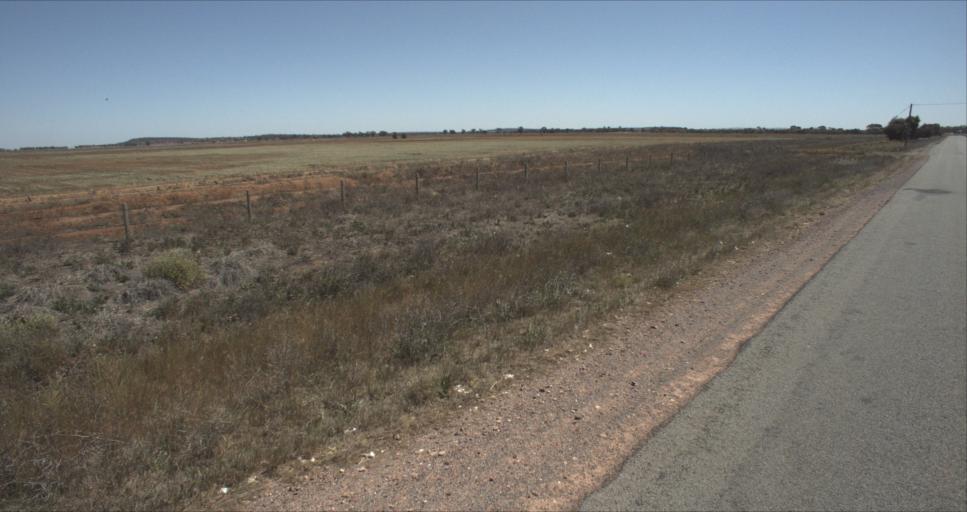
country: AU
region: New South Wales
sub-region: Leeton
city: Leeton
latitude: -34.4395
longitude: 146.2981
